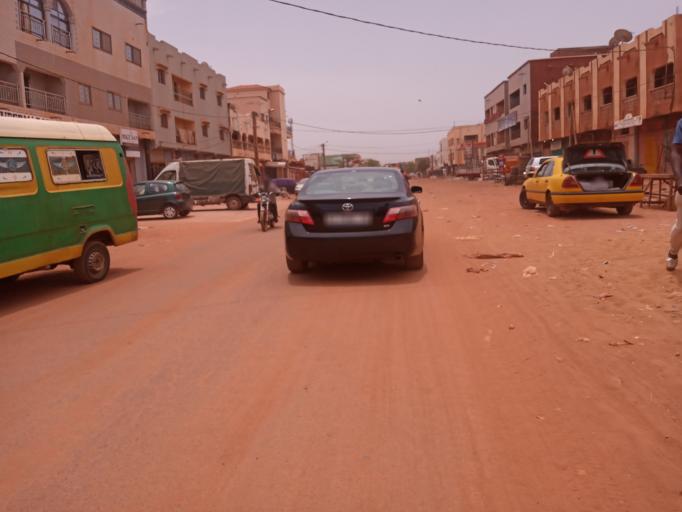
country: ML
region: Bamako
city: Bamako
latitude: 12.5780
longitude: -8.0141
